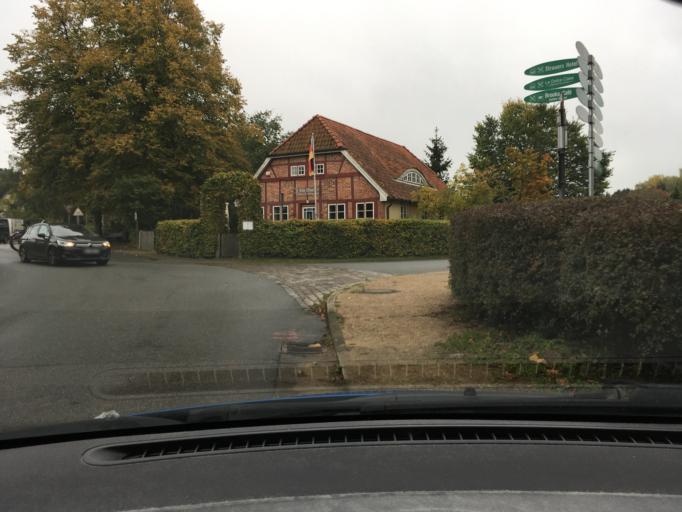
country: DE
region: Schleswig-Holstein
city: Bosau
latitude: 54.1045
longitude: 10.4295
